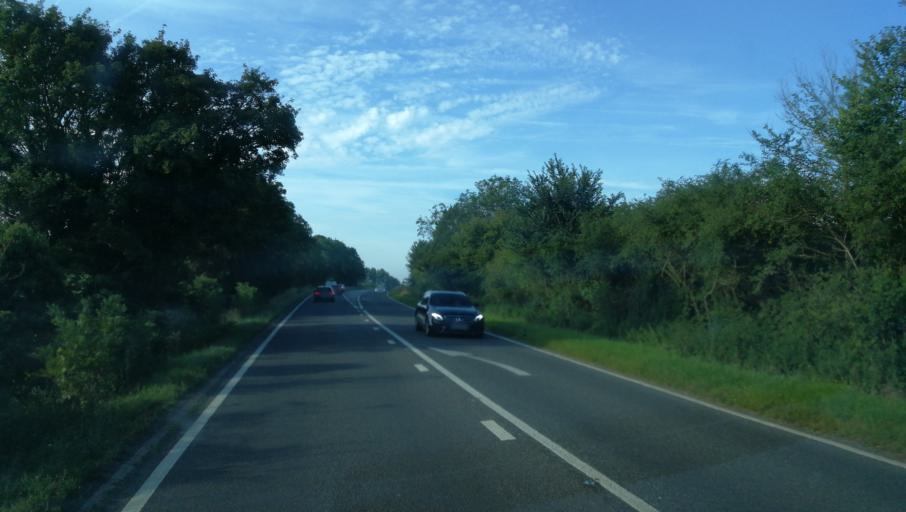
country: GB
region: England
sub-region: Oxfordshire
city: Deddington
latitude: 51.9517
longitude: -1.3187
